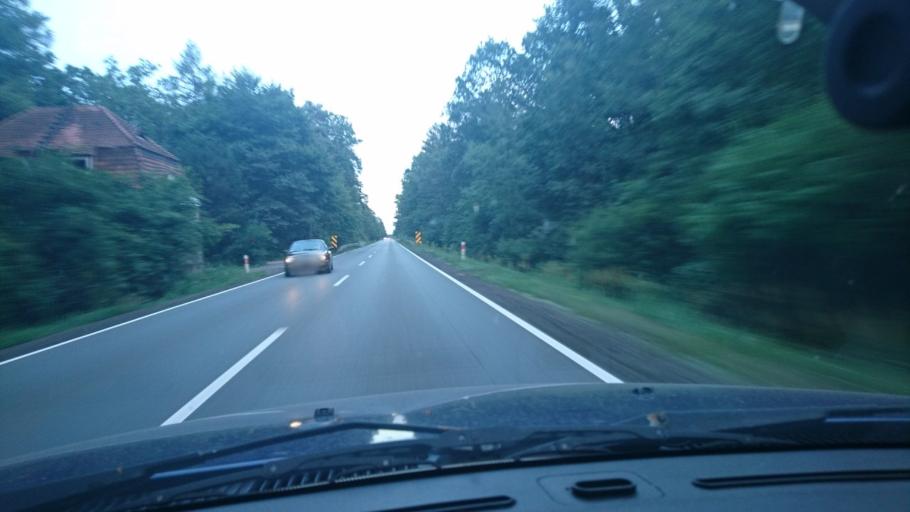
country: PL
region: Silesian Voivodeship
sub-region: Powiat tarnogorski
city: Tworog
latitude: 50.5113
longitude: 18.7452
